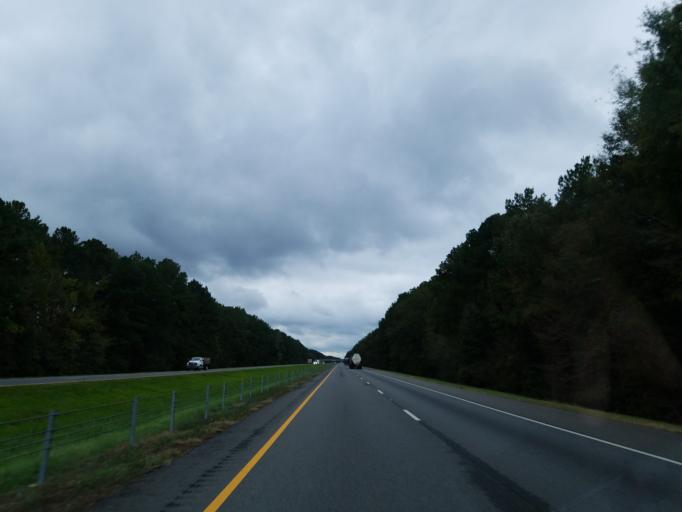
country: US
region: Alabama
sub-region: Greene County
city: Eutaw
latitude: 32.7673
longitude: -88.0644
